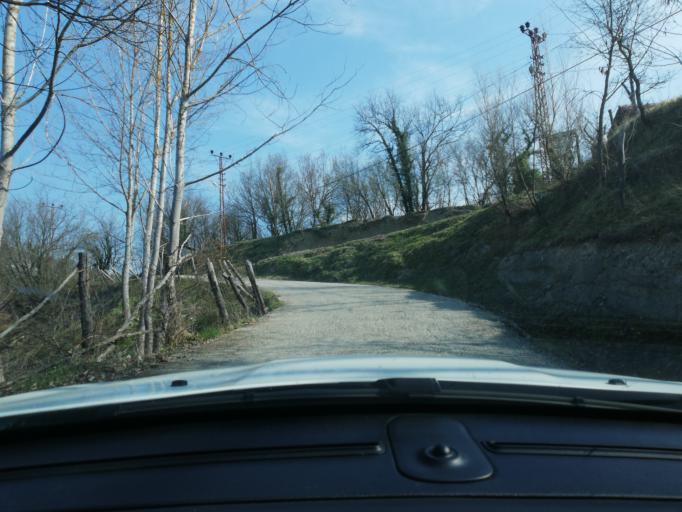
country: TR
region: Karabuk
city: Yenice
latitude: 41.2731
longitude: 32.3543
